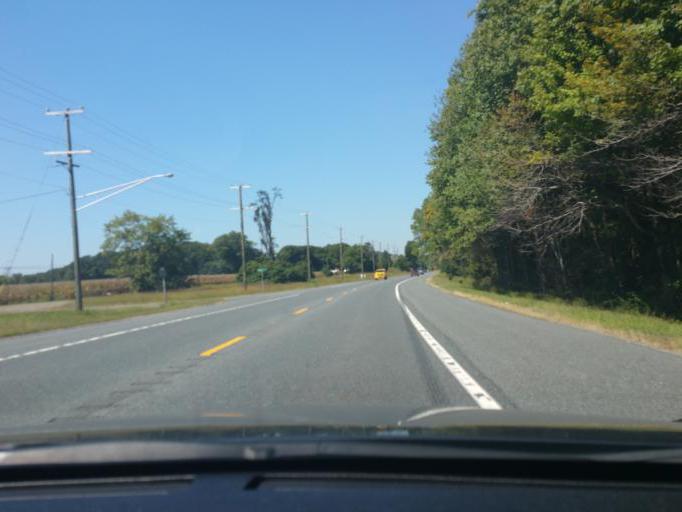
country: US
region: Maryland
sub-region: Harford County
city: Aberdeen
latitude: 39.5736
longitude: -76.1799
